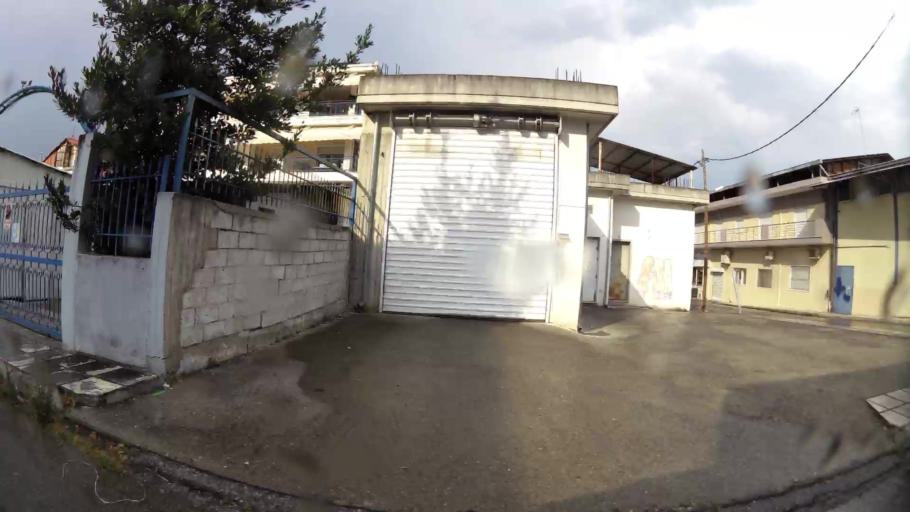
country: GR
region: Central Macedonia
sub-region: Nomos Imathias
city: Veroia
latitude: 40.5404
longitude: 22.2008
